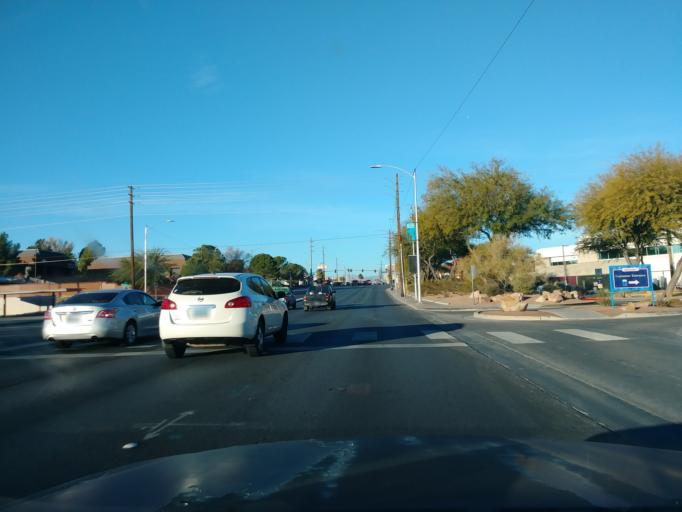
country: US
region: Nevada
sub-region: Clark County
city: Las Vegas
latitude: 36.1591
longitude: -115.1900
